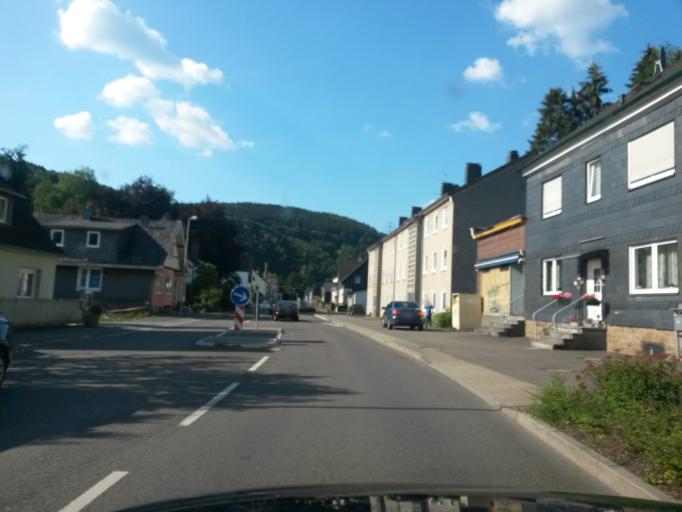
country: DE
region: North Rhine-Westphalia
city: Wiehl
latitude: 50.9907
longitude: 7.4907
